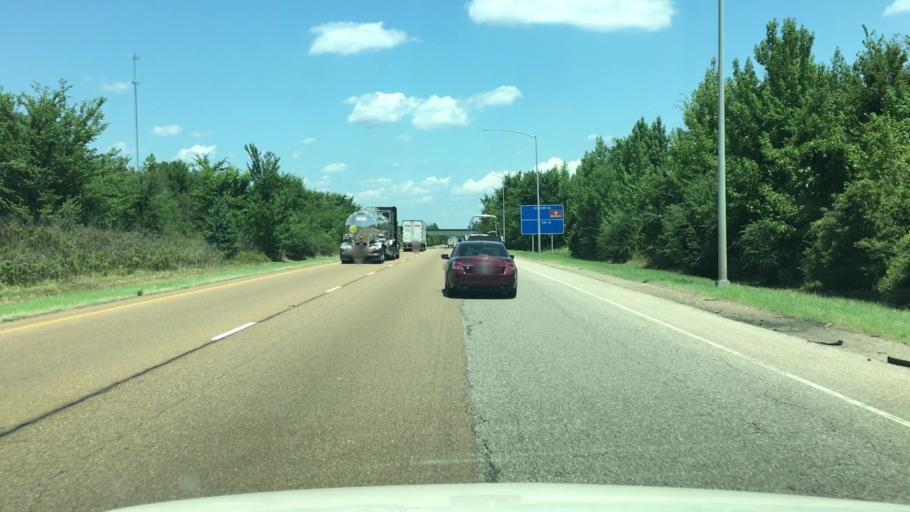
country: US
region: Arkansas
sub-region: Nevada County
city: Prescott
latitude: 33.8141
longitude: -93.4183
